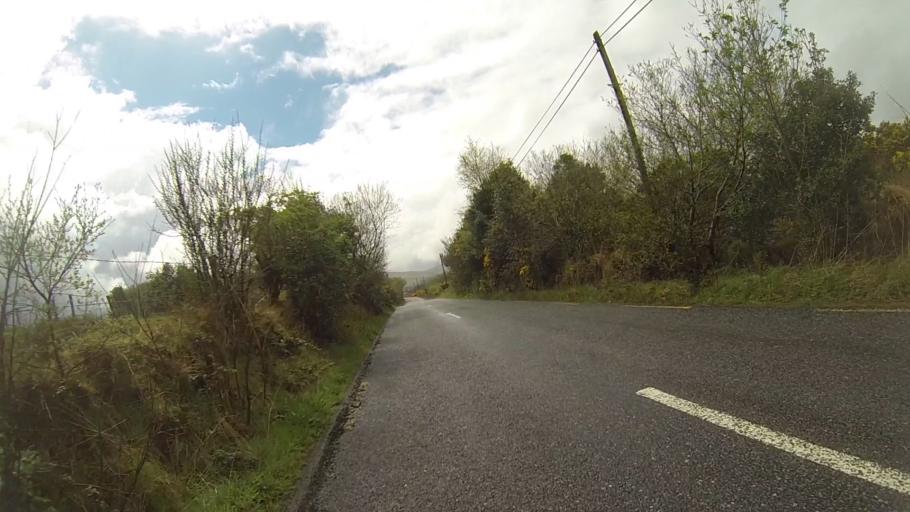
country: IE
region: Munster
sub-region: Ciarrai
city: Kenmare
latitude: 51.8992
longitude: -9.7506
